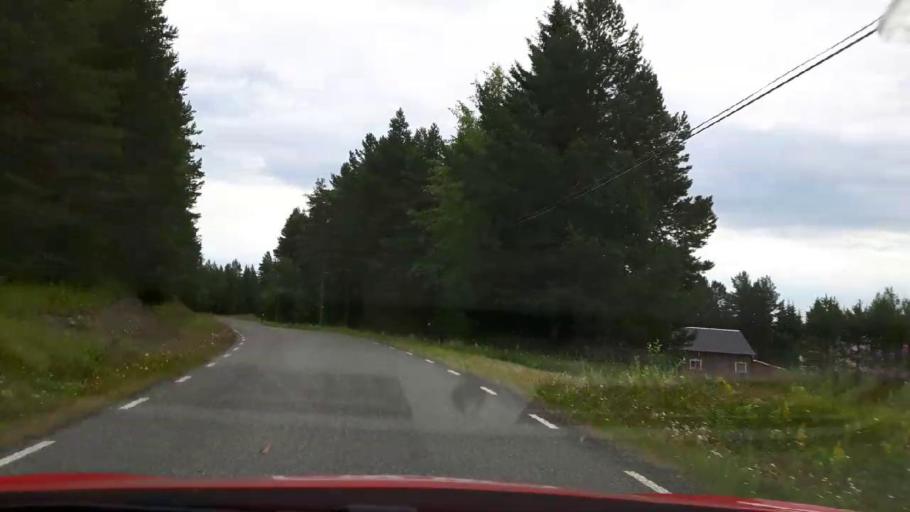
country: SE
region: Jaemtland
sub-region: OEstersunds Kommun
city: Lit
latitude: 63.3888
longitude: 15.0215
